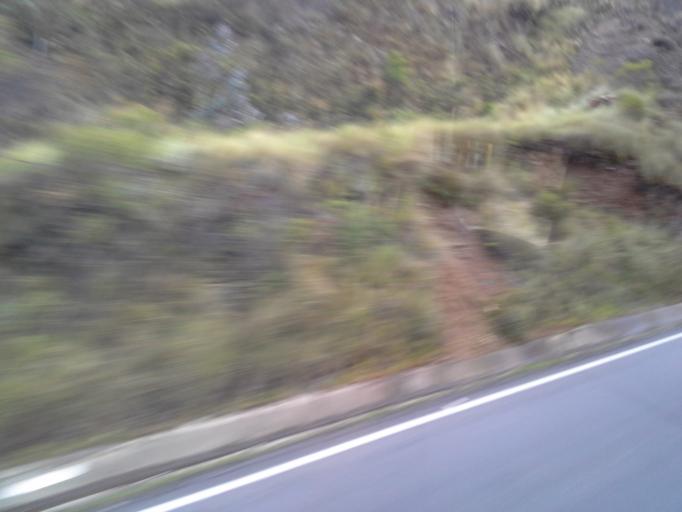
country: BO
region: Cochabamba
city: Colomi
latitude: -17.3933
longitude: -65.8515
